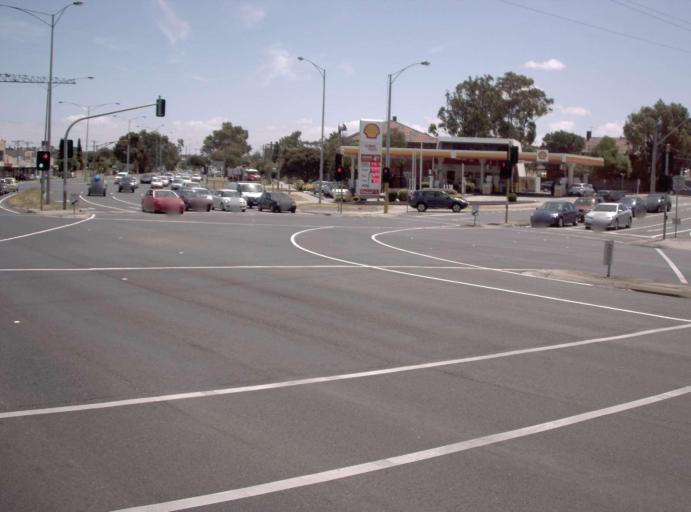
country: AU
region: Victoria
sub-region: Kingston
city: Mentone
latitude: -37.9823
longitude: 145.0715
